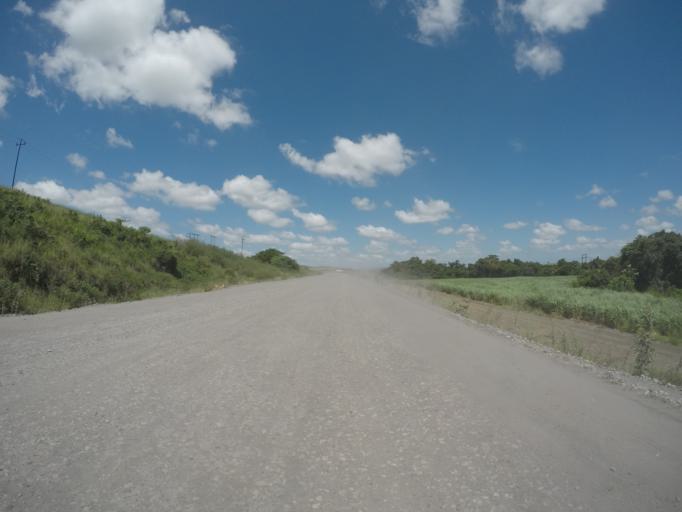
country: ZA
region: KwaZulu-Natal
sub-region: uThungulu District Municipality
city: Empangeni
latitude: -28.6558
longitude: 31.7699
